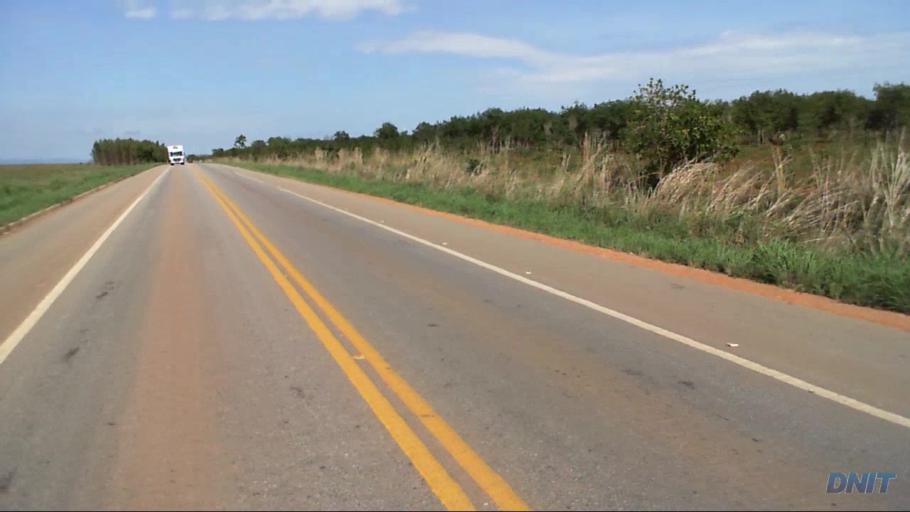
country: BR
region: Goias
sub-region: Barro Alto
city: Barro Alto
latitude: -15.2062
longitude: -48.7201
